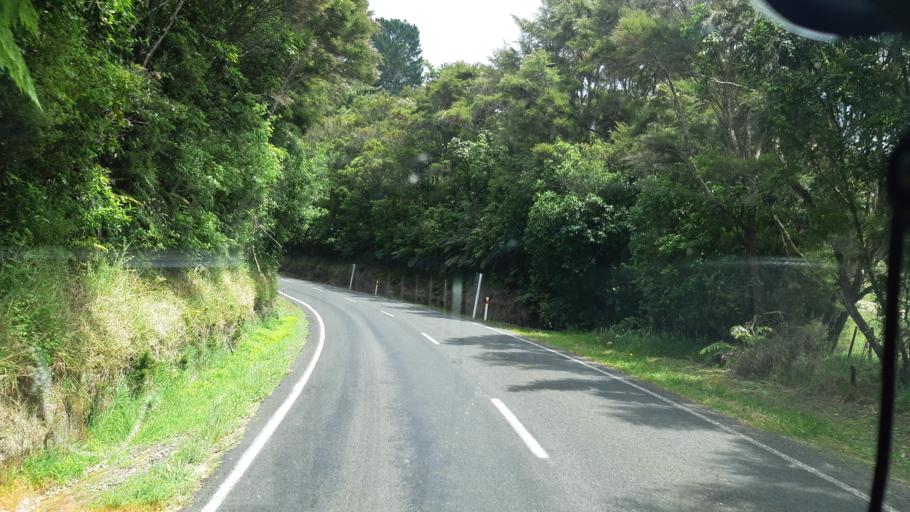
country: NZ
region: Waikato
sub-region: South Waikato District
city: Tokoroa
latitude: -38.2724
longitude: 175.6732
